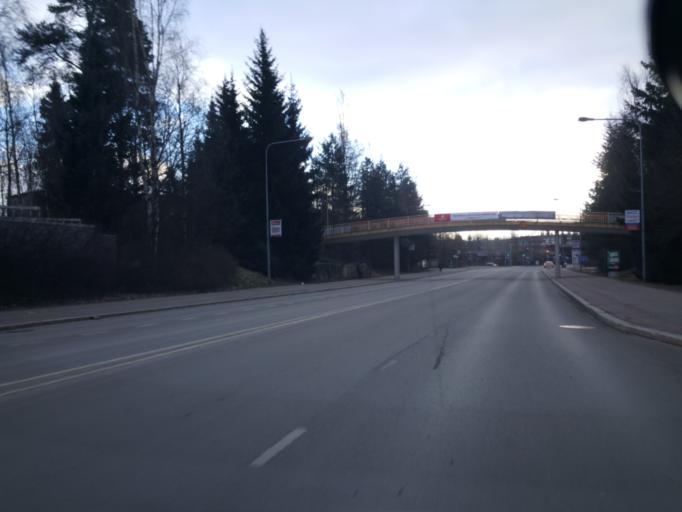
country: FI
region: Uusimaa
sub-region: Helsinki
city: Vantaa
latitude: 60.2992
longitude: 25.0336
